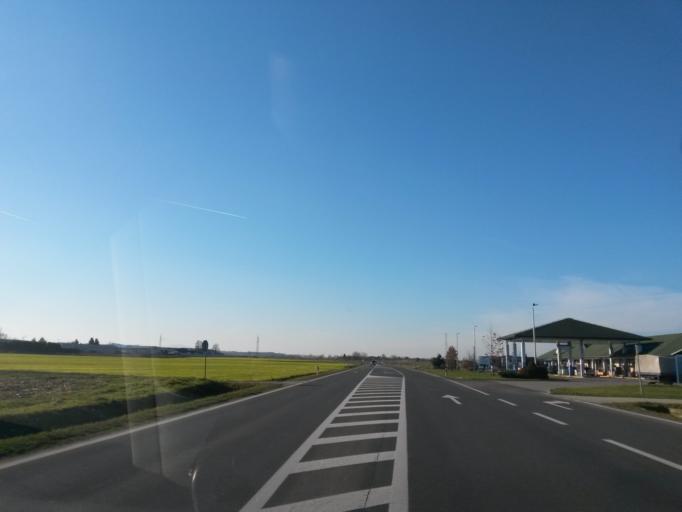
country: HR
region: Varazdinska
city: Ludbreg
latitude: 46.2584
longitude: 16.6077
